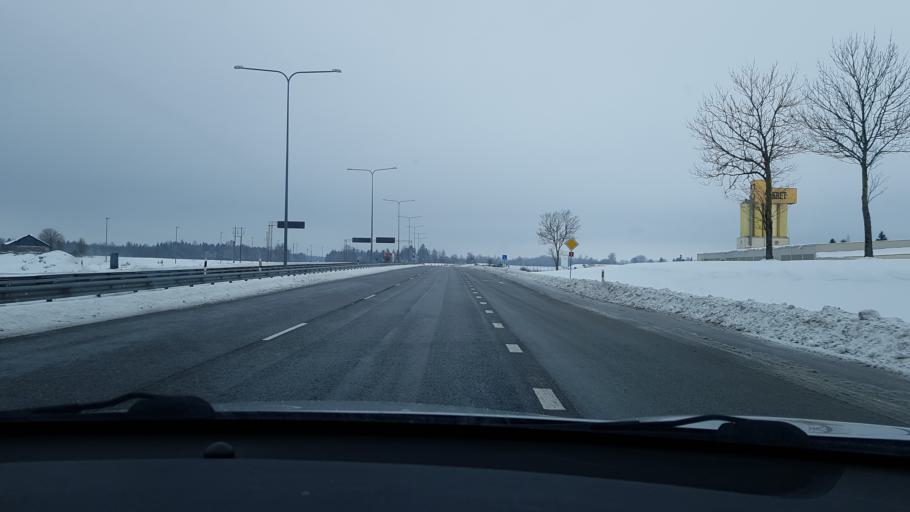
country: EE
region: Jaervamaa
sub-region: Paide linn
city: Paide
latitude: 58.9158
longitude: 25.6078
